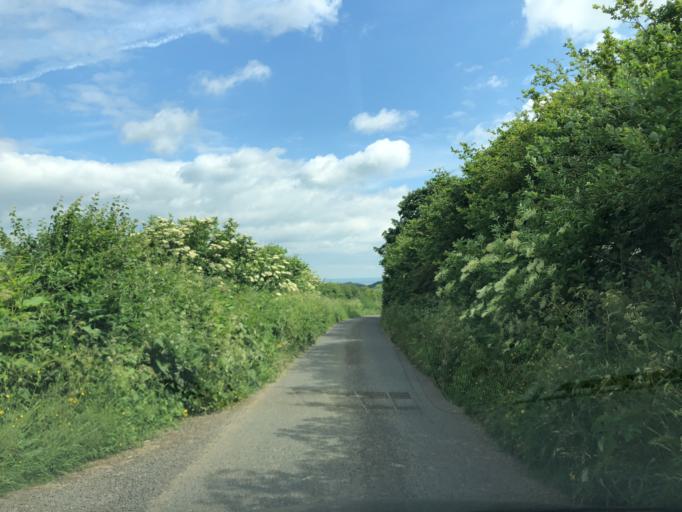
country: GB
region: England
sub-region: North Yorkshire
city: Helmsley
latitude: 54.1504
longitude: -1.0116
